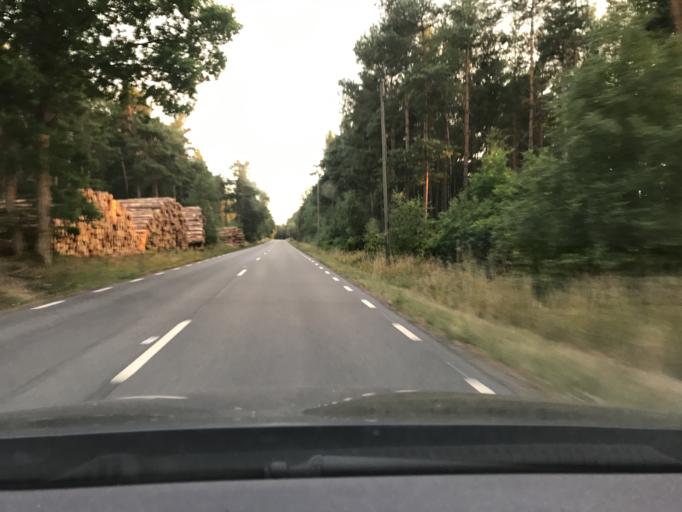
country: SE
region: Skane
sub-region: Simrishamns Kommun
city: Simrishamn
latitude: 55.4003
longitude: 14.1823
